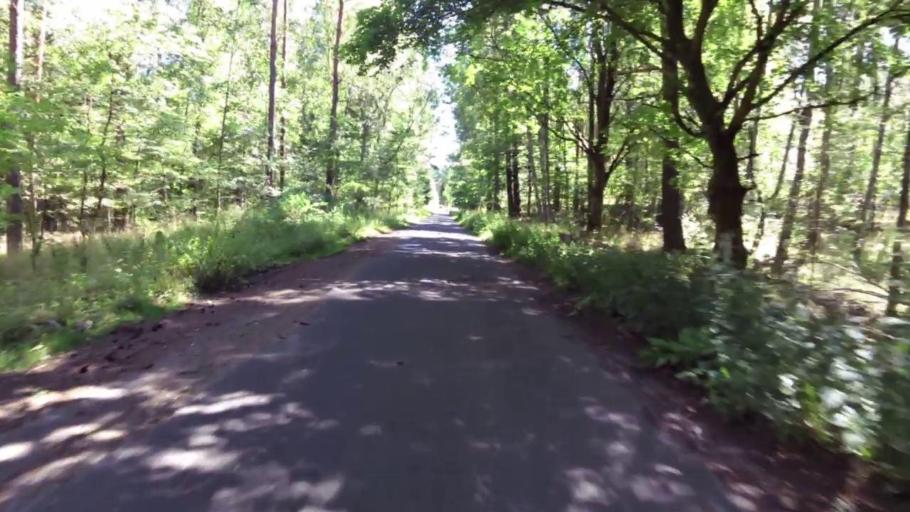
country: PL
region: West Pomeranian Voivodeship
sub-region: Powiat szczecinecki
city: Borne Sulinowo
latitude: 53.5999
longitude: 16.6135
